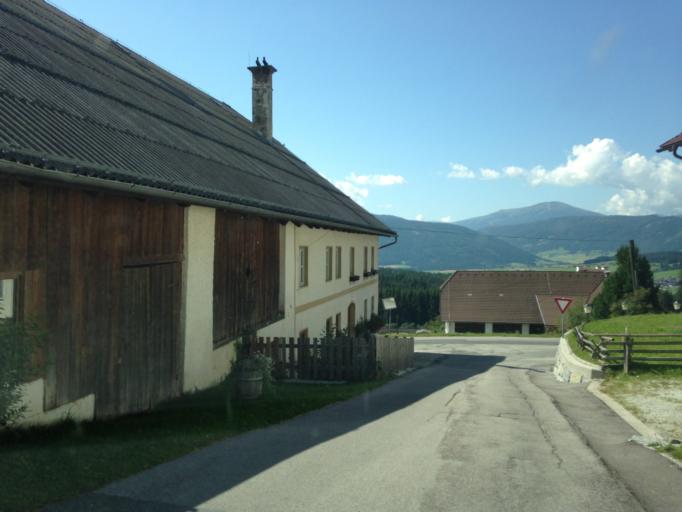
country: AT
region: Salzburg
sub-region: Politischer Bezirk Tamsweg
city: Mariapfarr
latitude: 47.1719
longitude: 13.7312
